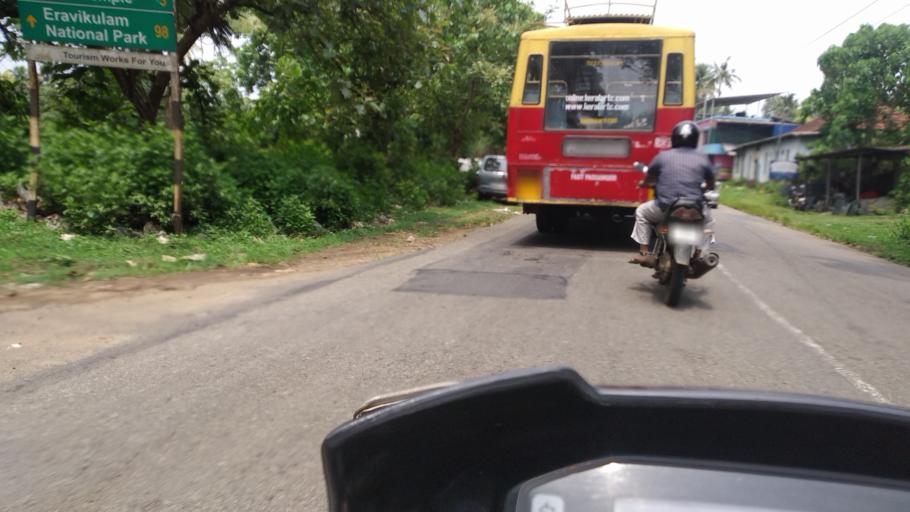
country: IN
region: Kerala
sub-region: Ernakulam
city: Perumpavur
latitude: 10.0960
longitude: 76.5531
